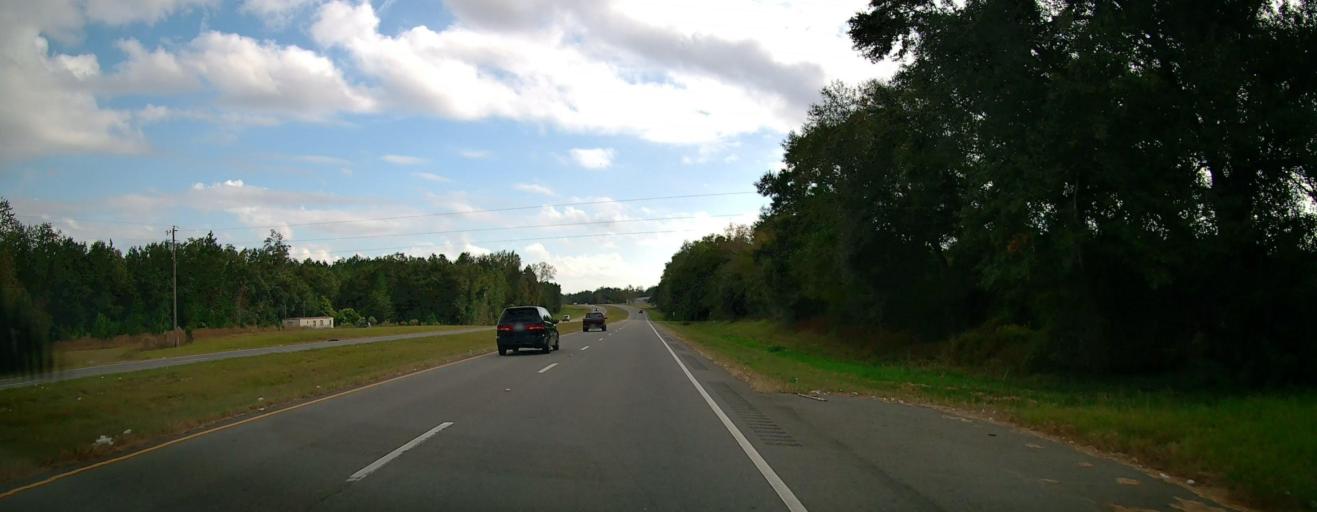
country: US
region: Georgia
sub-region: Thomas County
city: Meigs
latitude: 31.0519
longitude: -84.0712
